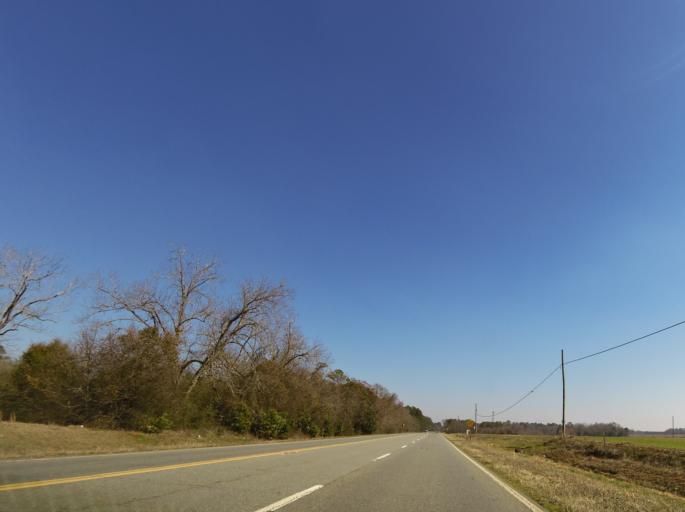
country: US
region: Georgia
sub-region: Bleckley County
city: Cochran
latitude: 32.3608
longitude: -83.3862
